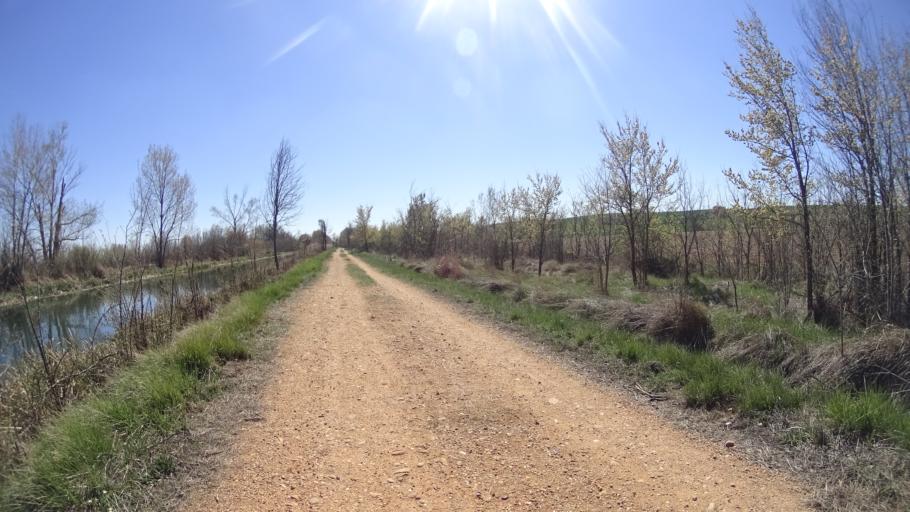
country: ES
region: Castille and Leon
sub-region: Provincia de Burgos
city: Melgar de Fernamental
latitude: 42.4464
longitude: -4.2649
